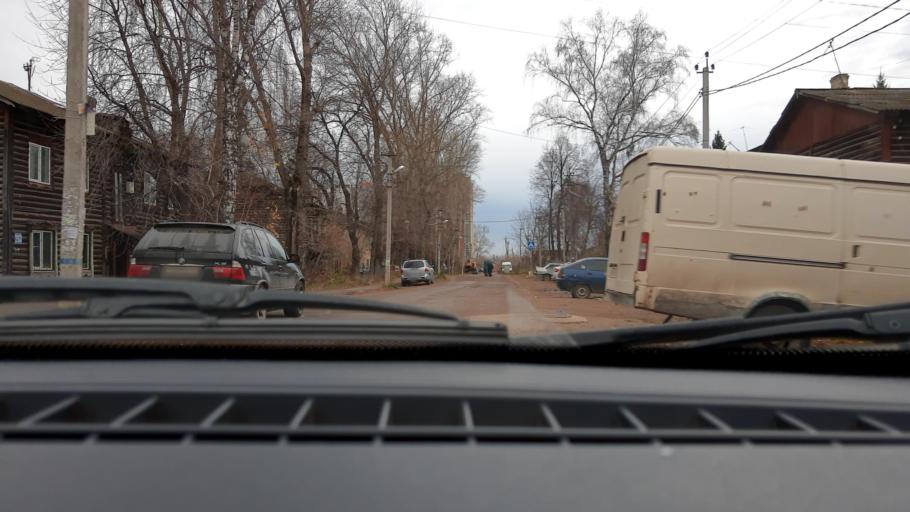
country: RU
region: Bashkortostan
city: Mikhaylovka
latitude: 54.7825
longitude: 55.8849
